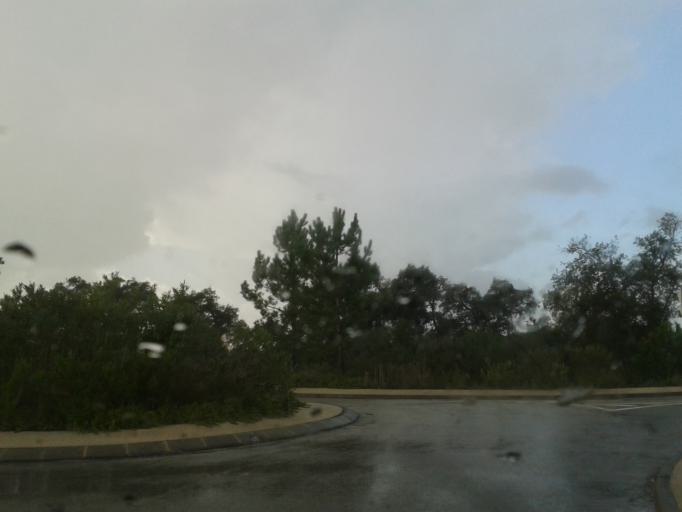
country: PT
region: Santarem
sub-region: Benavente
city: Poceirao
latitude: 38.8277
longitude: -8.7511
